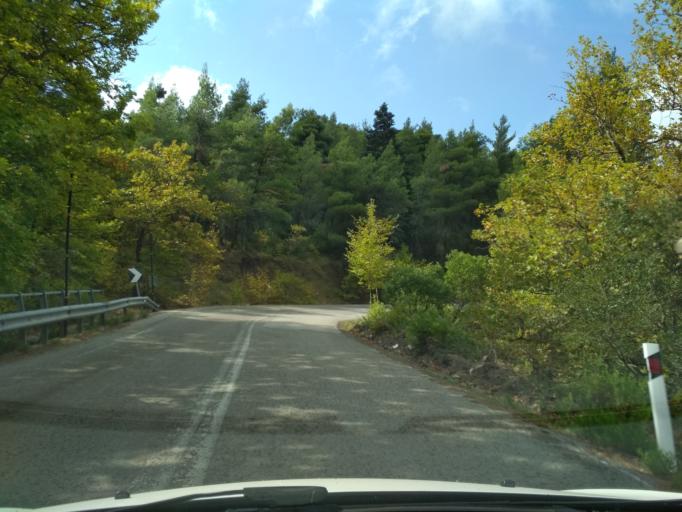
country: GR
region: Central Greece
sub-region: Nomos Evvoias
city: Politika
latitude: 38.6629
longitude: 23.5592
